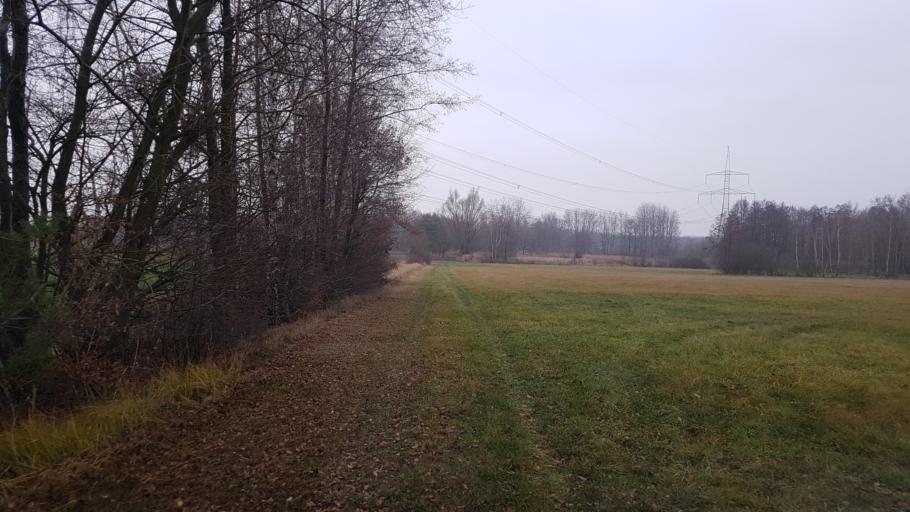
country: DE
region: Brandenburg
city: Doberlug-Kirchhain
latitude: 51.6296
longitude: 13.5349
